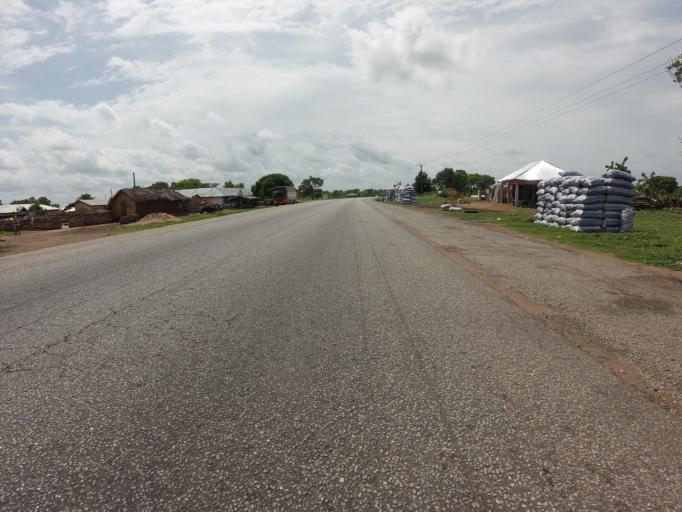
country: GH
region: Brong-Ahafo
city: Kintampo
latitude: 8.4510
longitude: -1.5656
